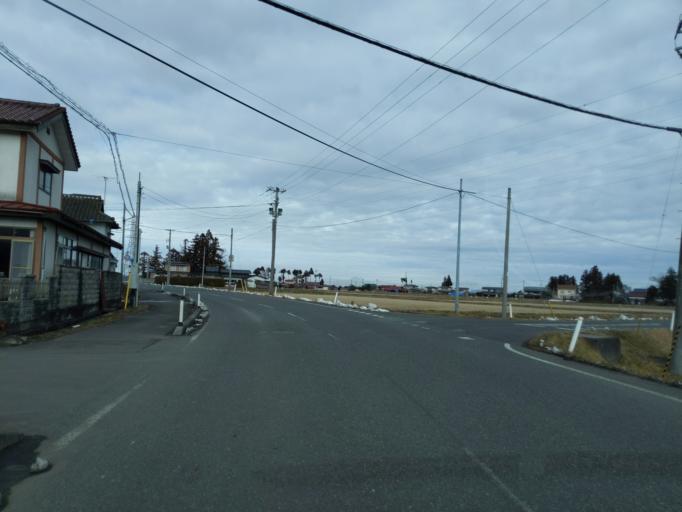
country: JP
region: Iwate
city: Mizusawa
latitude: 39.0752
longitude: 141.1630
